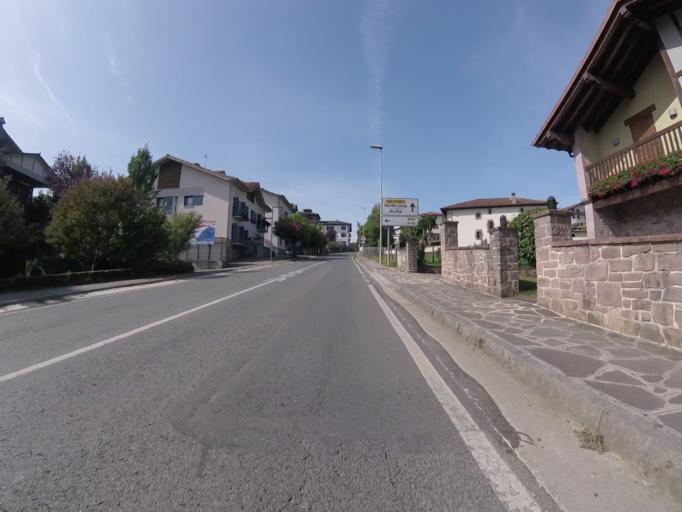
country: ES
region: Navarre
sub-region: Provincia de Navarra
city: Doneztebe
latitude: 43.1319
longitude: -1.5450
